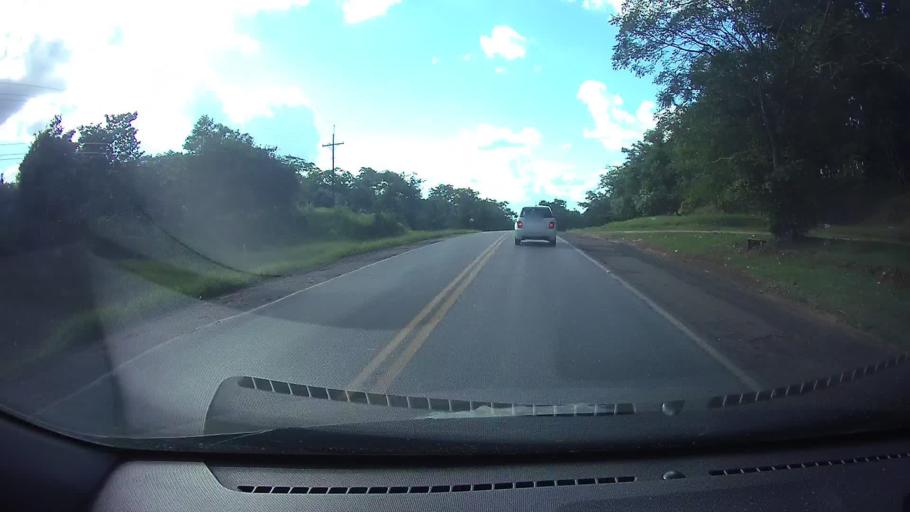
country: PY
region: Cordillera
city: Eusebio Ayala
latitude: -25.4160
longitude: -56.9307
